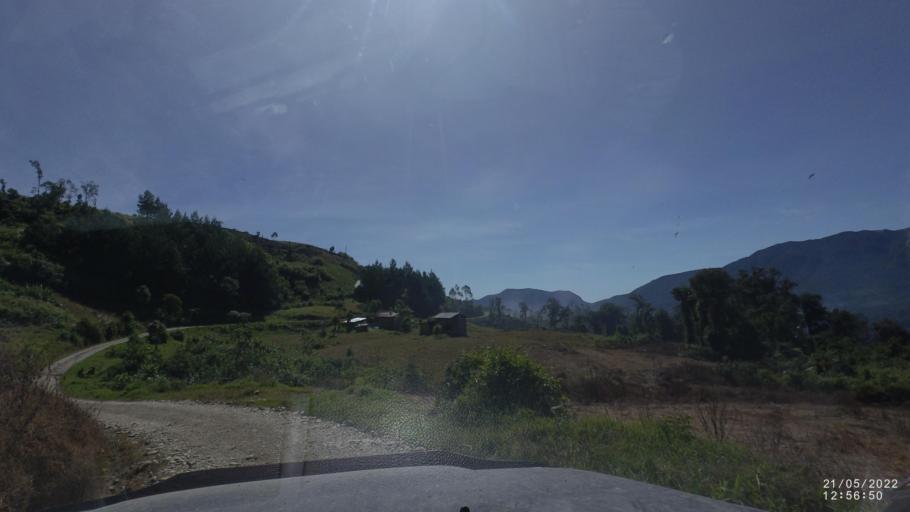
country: BO
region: Cochabamba
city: Colomi
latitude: -17.1720
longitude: -65.9451
